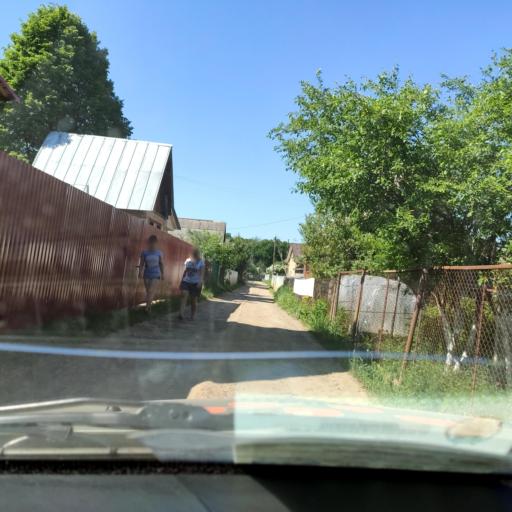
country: RU
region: Bashkortostan
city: Ufa
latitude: 54.7878
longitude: 56.1837
